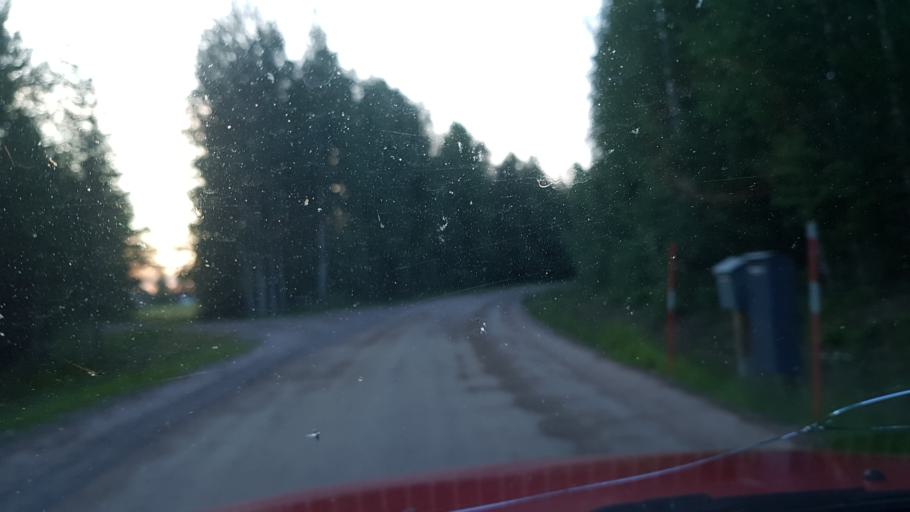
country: SE
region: Norrbotten
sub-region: Alvsbyns Kommun
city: AElvsbyn
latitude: 65.6968
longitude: 20.6696
